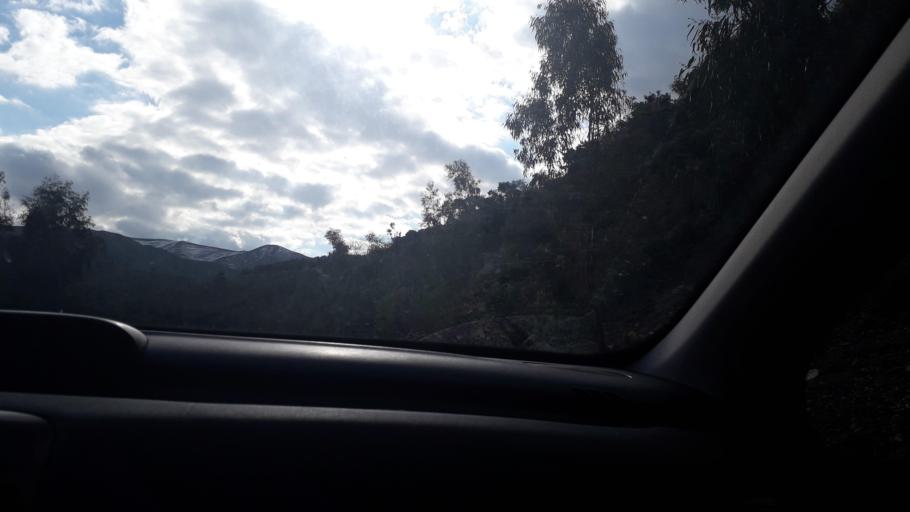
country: GR
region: Crete
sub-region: Nomos Rethymnis
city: Agia Foteini
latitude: 35.2852
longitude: 24.5630
